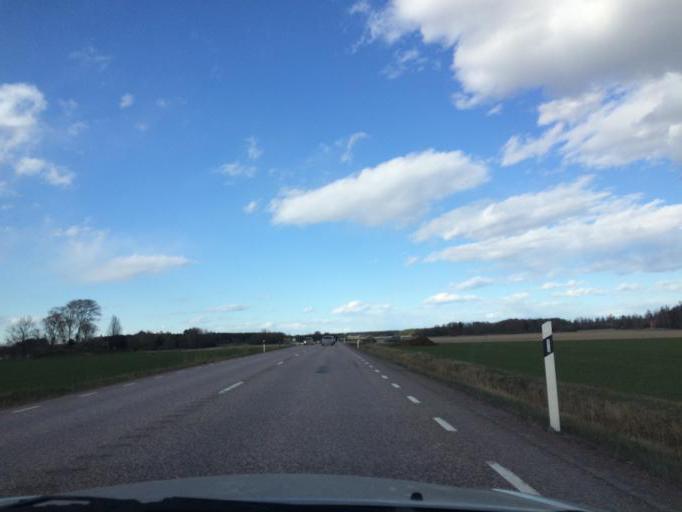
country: SE
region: Vaestmanland
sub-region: Hallstahammars Kommun
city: Kolback
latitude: 59.5385
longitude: 16.3241
